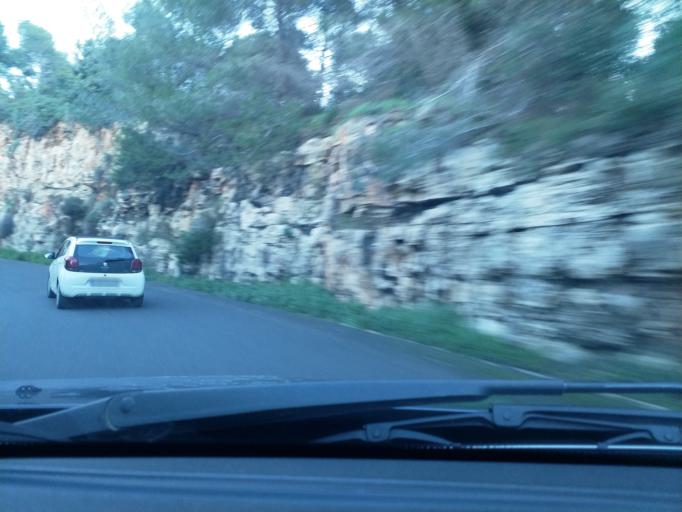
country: GR
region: Crete
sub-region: Nomos Chanias
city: Chania
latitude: 35.5194
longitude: 24.0573
